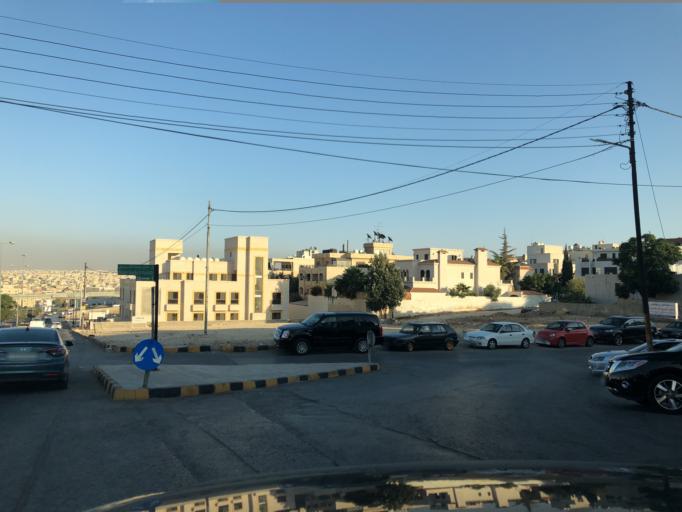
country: JO
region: Amman
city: Al Bunayyat ash Shamaliyah
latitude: 31.9411
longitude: 35.8849
